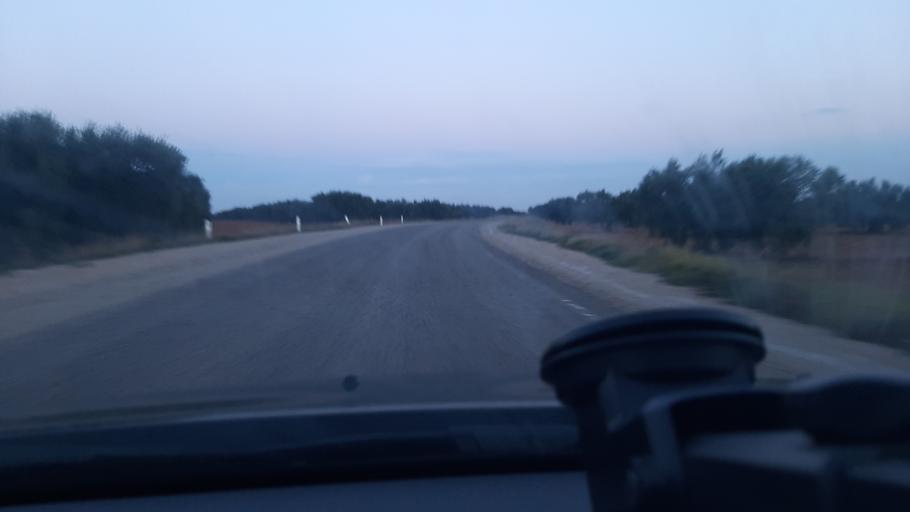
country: TN
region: Al Mahdiyah
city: Shurban
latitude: 35.0291
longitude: 10.4797
